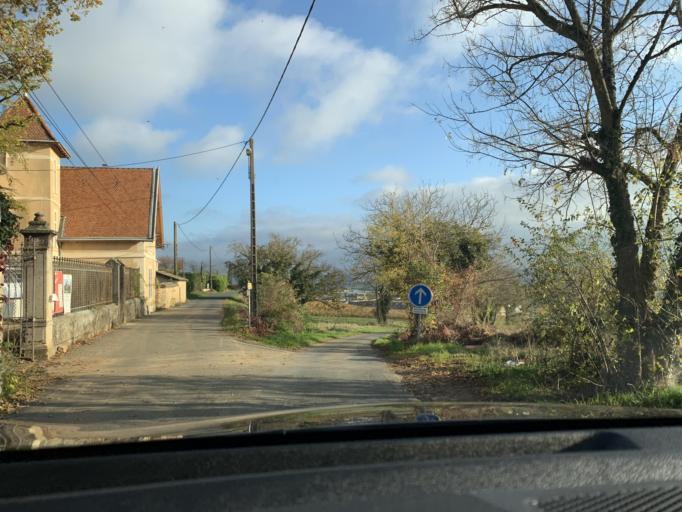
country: FR
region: Rhone-Alpes
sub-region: Departement du Rhone
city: Pommiers
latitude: 45.9582
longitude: 4.7100
